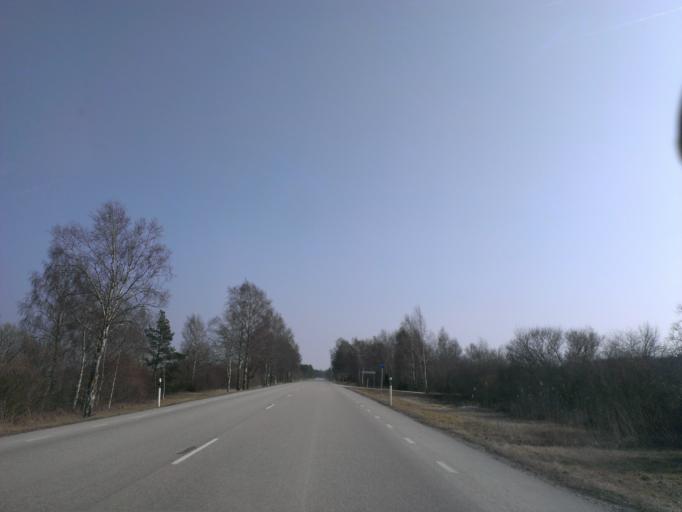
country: EE
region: Saare
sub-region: Orissaare vald
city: Orissaare
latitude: 58.5550
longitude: 23.1009
